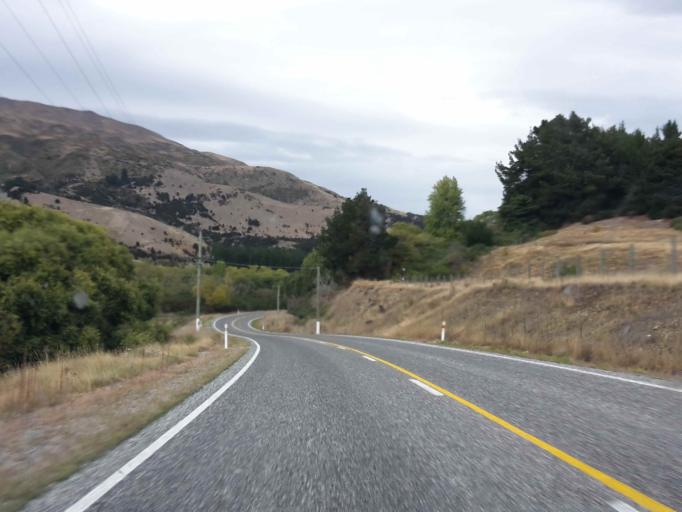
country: NZ
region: Otago
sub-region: Queenstown-Lakes District
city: Wanaka
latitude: -44.7425
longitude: 169.1304
